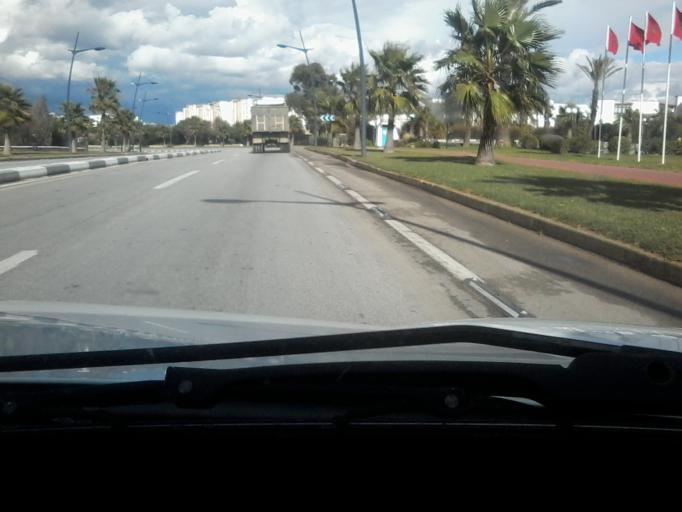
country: ES
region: Ceuta
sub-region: Ceuta
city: Ceuta
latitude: 35.7512
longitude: -5.3458
